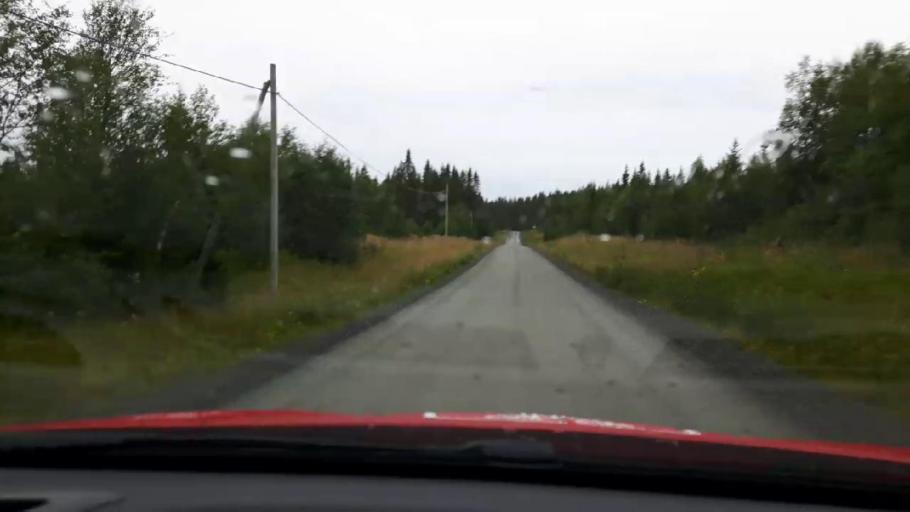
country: SE
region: Jaemtland
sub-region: Are Kommun
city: Are
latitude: 63.4834
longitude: 12.7926
